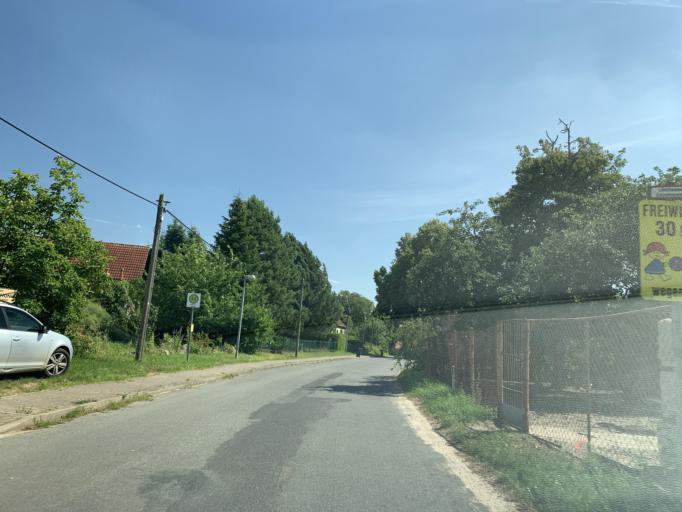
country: DE
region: Mecklenburg-Vorpommern
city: Carpin
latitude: 53.3259
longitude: 13.2402
